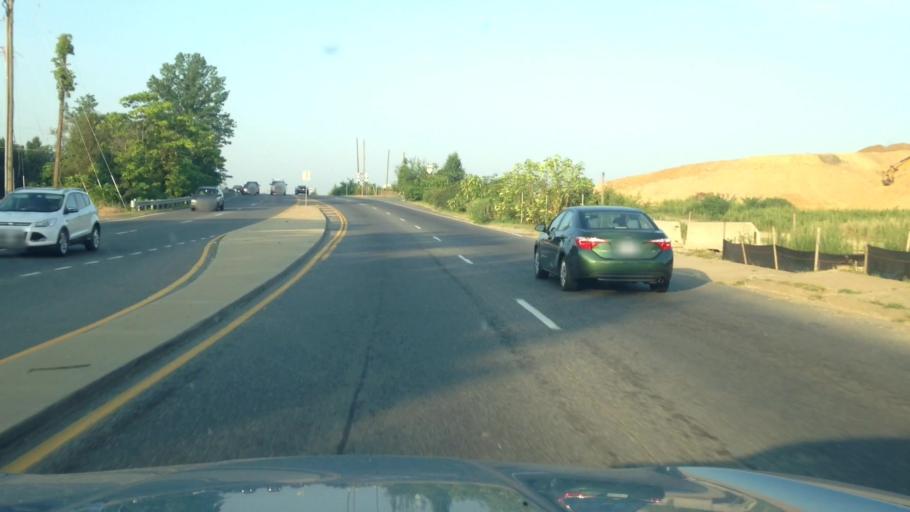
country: US
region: Virginia
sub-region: Prince William County
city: Woodbridge
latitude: 38.6646
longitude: -77.2446
